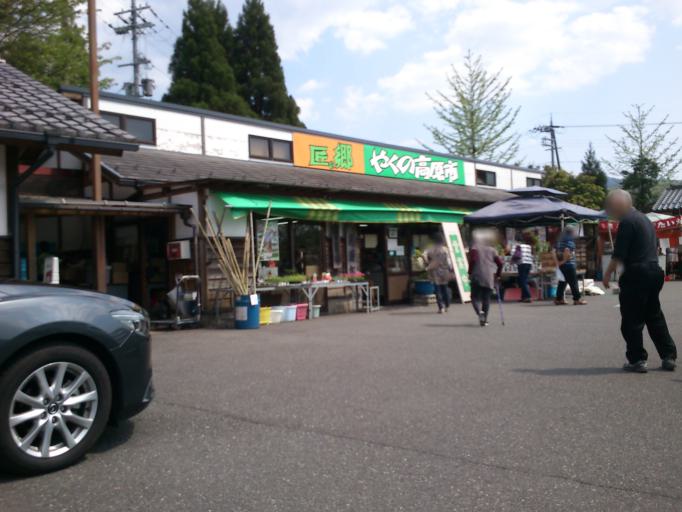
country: JP
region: Kyoto
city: Fukuchiyama
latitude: 35.3385
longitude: 134.9294
